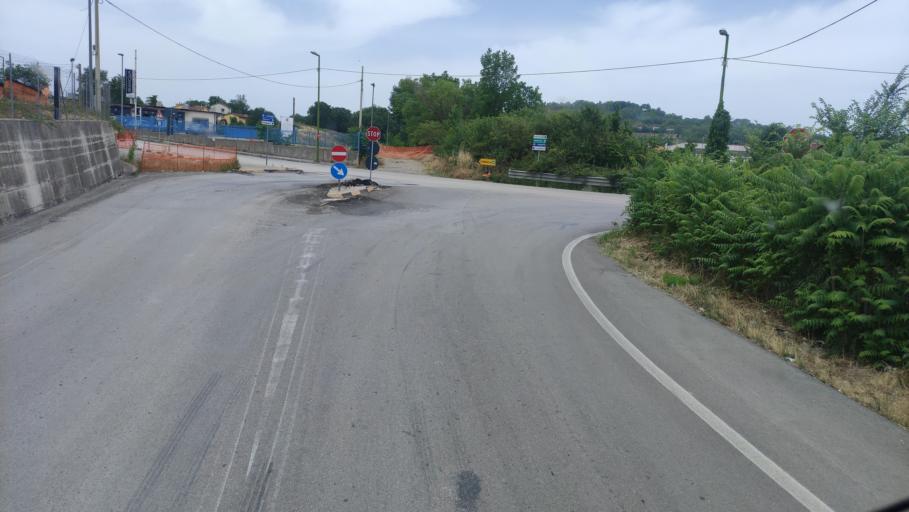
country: IT
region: Campania
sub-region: Provincia di Avellino
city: Grottaminarda
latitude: 41.0633
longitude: 15.0584
